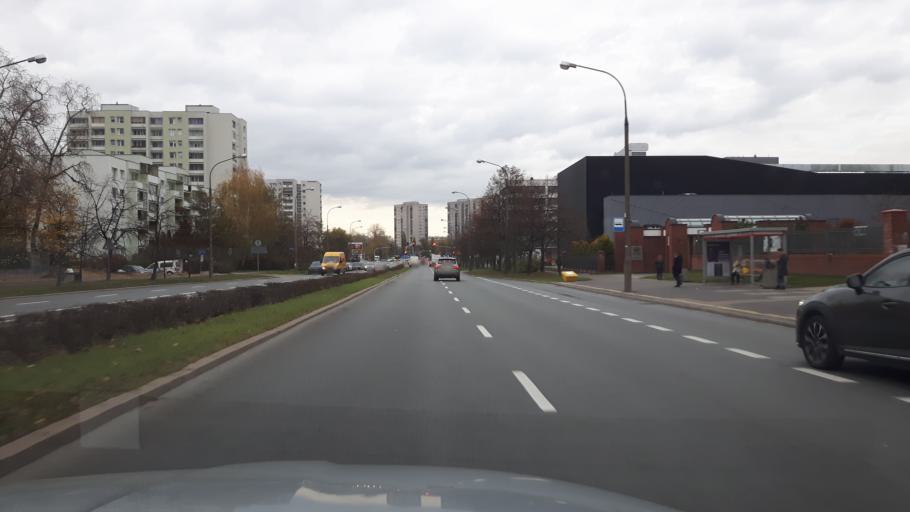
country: PL
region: Masovian Voivodeship
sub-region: Warszawa
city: Ursynow
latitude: 52.1480
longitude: 21.0427
